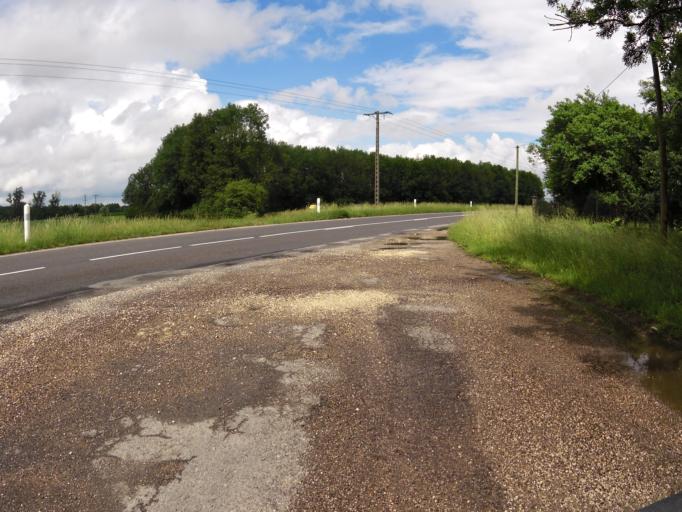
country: FR
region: Lorraine
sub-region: Departement de la Meuse
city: Revigny-sur-Ornain
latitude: 48.8123
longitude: 4.9700
